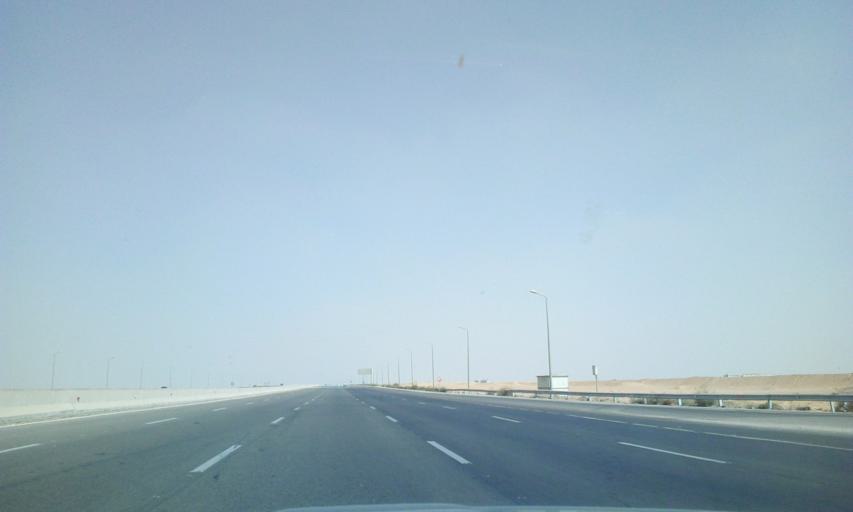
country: EG
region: Muhafazat al Qahirah
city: Halwan
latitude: 29.9056
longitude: 31.6999
